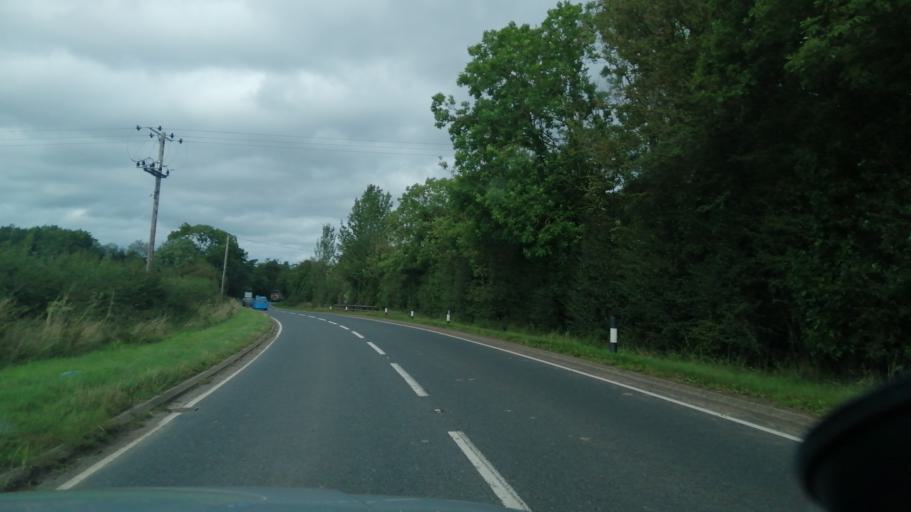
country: GB
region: Wales
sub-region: Monmouthshire
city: Grosmont
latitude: 51.9581
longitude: -2.8558
